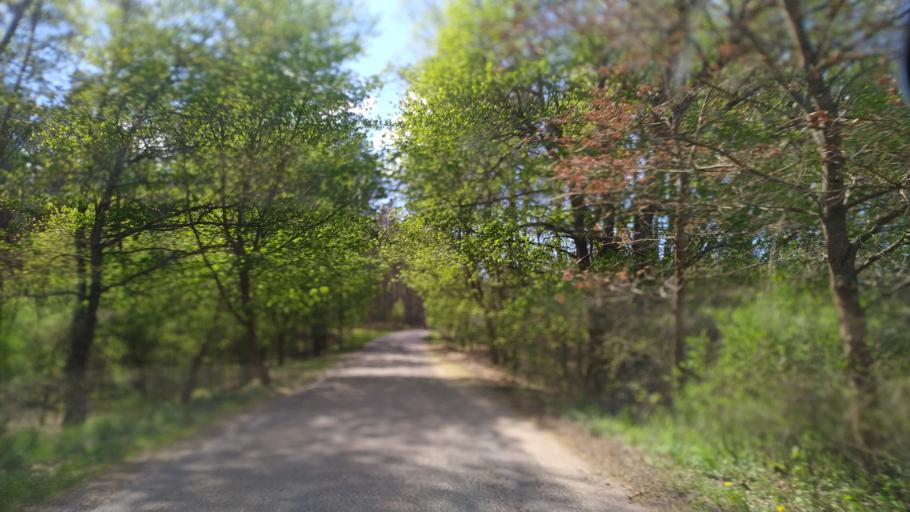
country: PL
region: Greater Poland Voivodeship
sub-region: Powiat pilski
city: Pila
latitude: 53.2545
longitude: 16.7420
